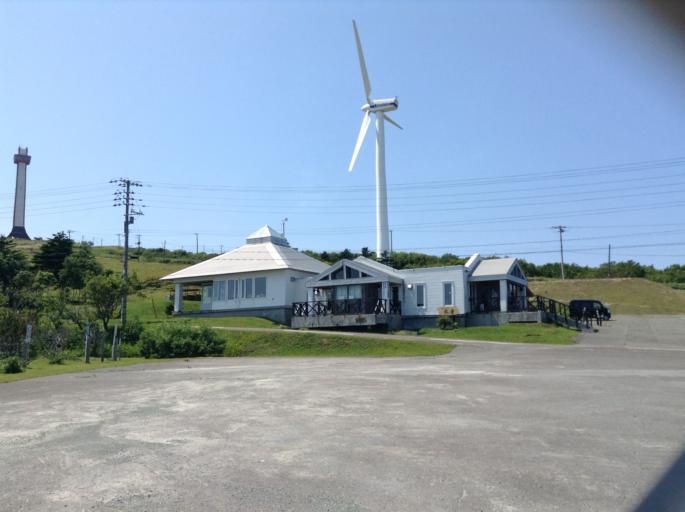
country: JP
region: Hokkaido
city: Wakkanai
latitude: 45.4182
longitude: 141.6699
